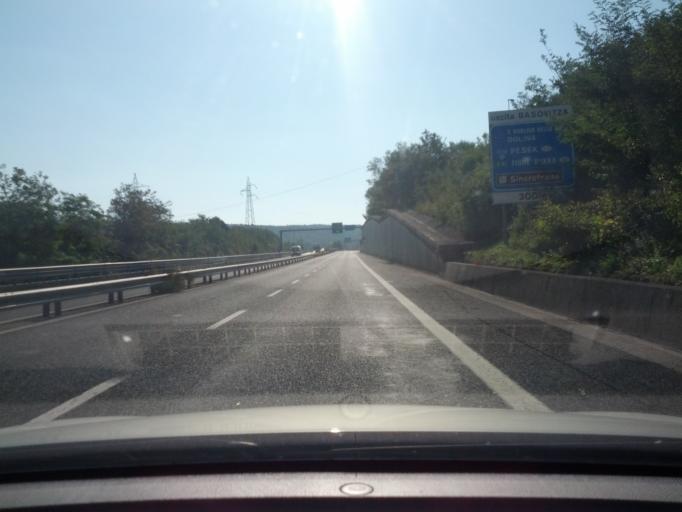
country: IT
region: Friuli Venezia Giulia
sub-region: Provincia di Trieste
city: Trieste
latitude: 45.6368
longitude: 13.8175
